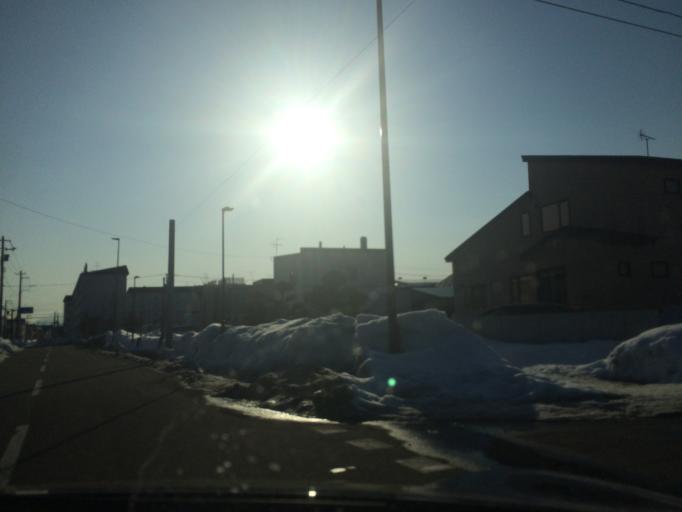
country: JP
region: Hokkaido
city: Chitose
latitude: 42.8809
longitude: 141.5864
